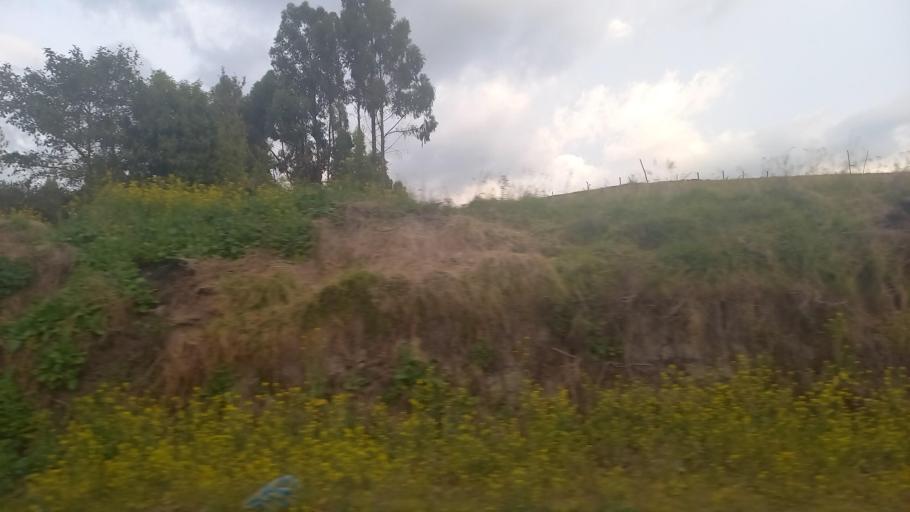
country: EC
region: Pichincha
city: Cayambe
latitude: 0.0899
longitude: -78.1007
